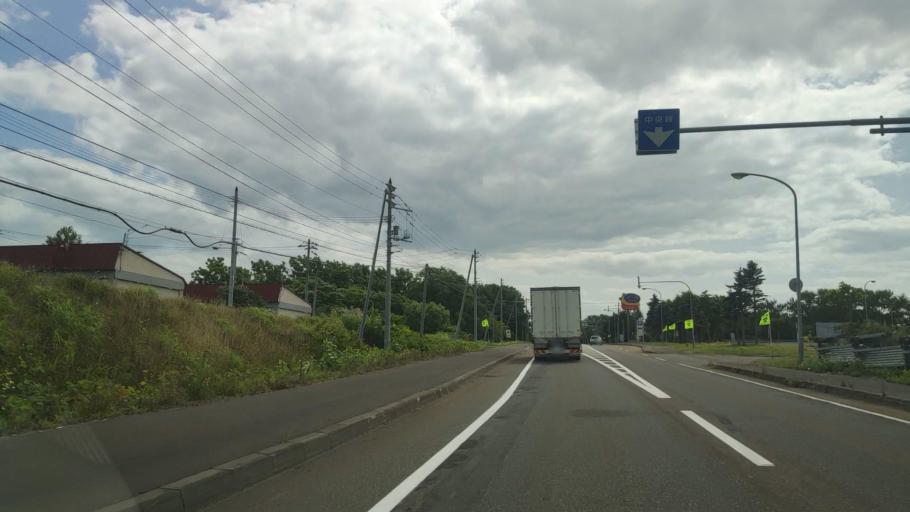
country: JP
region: Hokkaido
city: Rumoi
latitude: 44.5641
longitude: 141.7859
